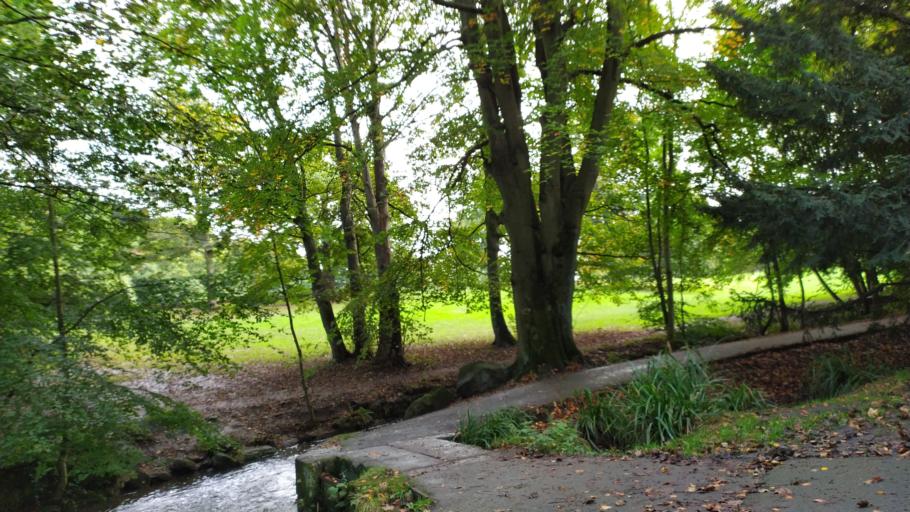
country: GB
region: England
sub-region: City and Borough of Leeds
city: Chapel Allerton
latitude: 53.8338
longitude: -1.5770
